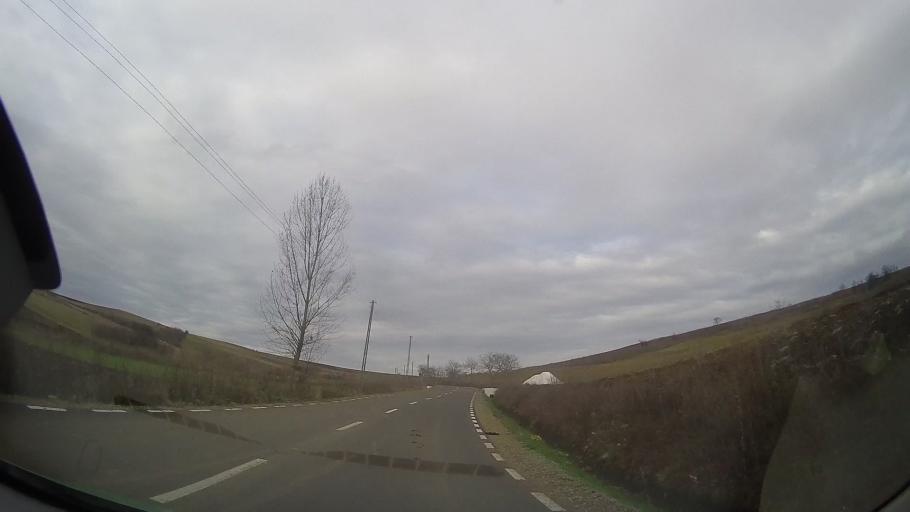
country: RO
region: Mures
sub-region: Comuna Cozma
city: Cozma
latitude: 46.8180
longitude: 24.4888
